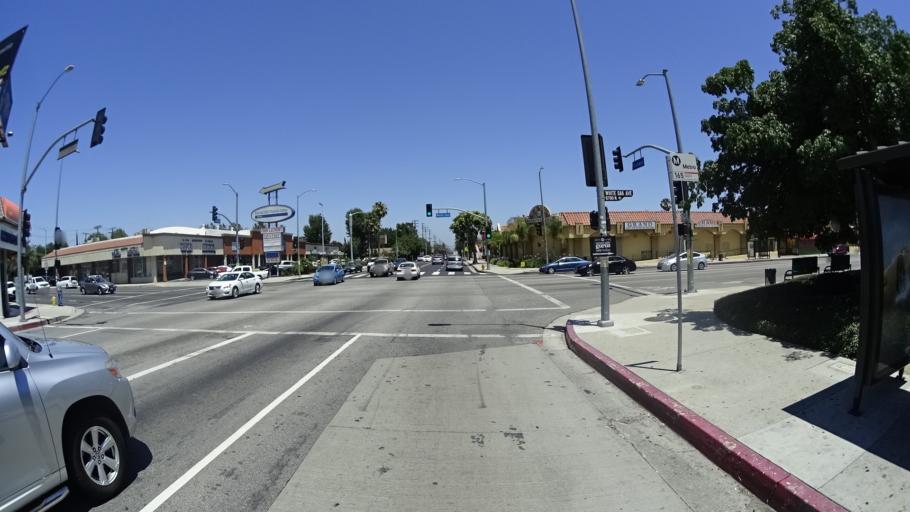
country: US
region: California
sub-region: Los Angeles County
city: Northridge
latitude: 34.1938
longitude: -118.5189
